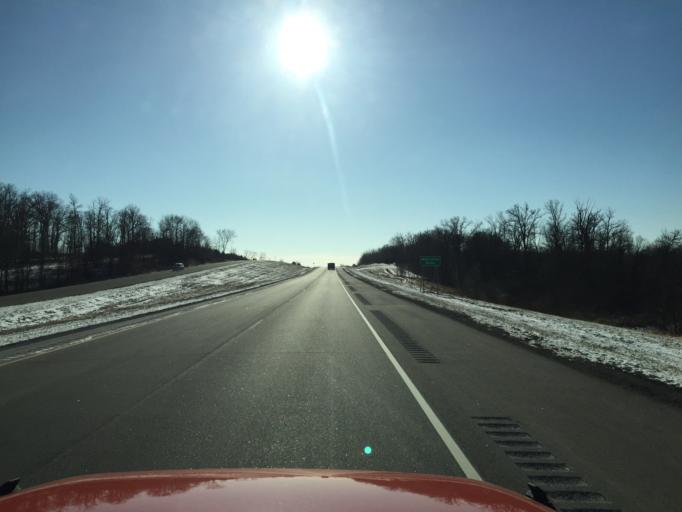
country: US
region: Minnesota
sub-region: Mille Lacs County
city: Milaca
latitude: 45.8142
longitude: -93.6554
